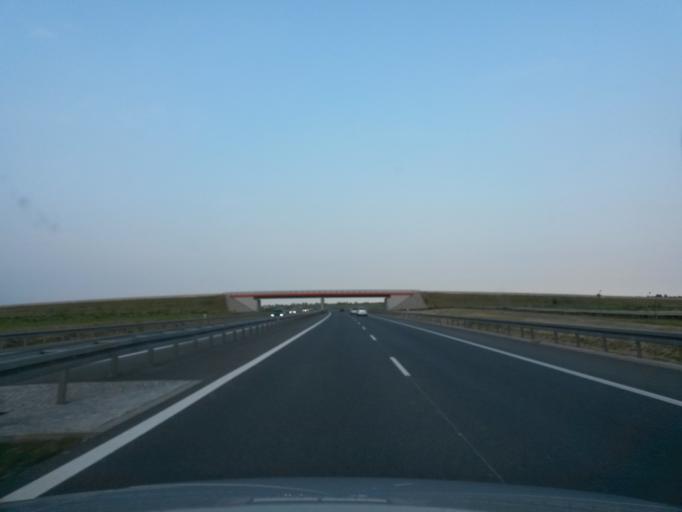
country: PL
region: Lower Silesian Voivodeship
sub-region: Powiat olesnicki
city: Dobroszyce
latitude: 51.2218
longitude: 17.3161
